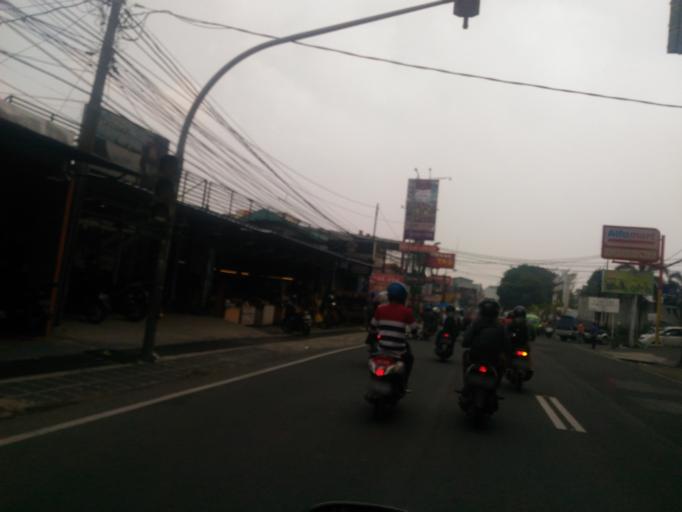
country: ID
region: West Java
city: Bogor
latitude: -6.6237
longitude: 106.8192
